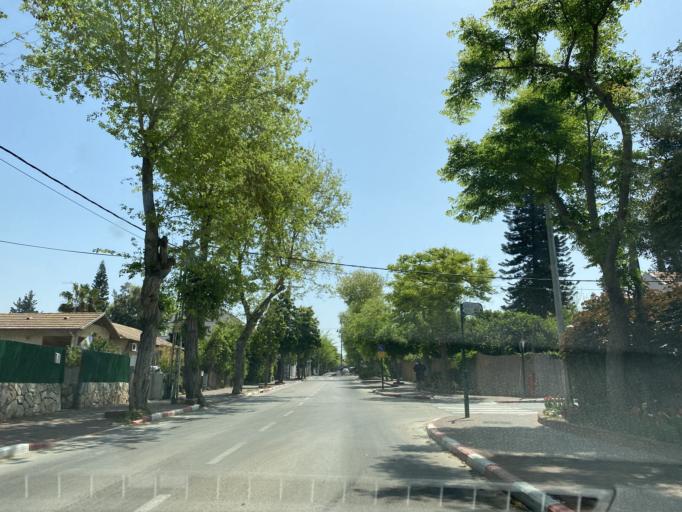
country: IL
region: Central District
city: Ra'anana
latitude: 32.1867
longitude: 34.8741
